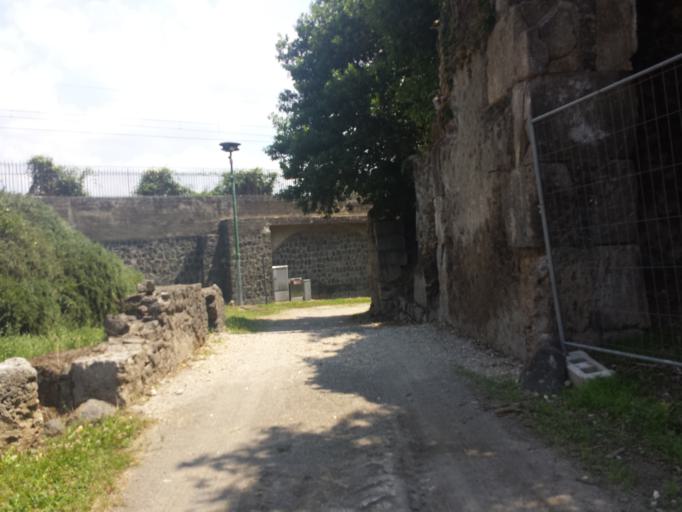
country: IT
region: Campania
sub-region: Provincia di Napoli
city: Pompei
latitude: 40.7528
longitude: 14.4944
